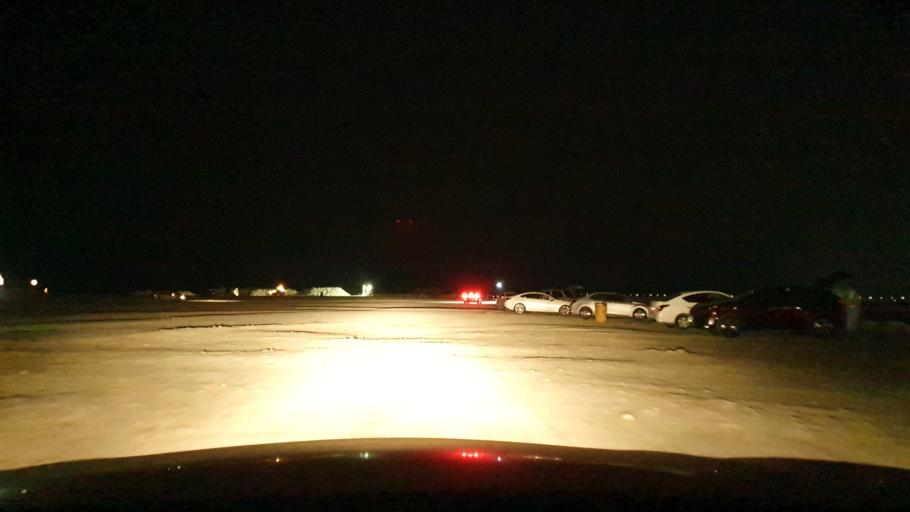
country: BH
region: Muharraq
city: Al Muharraq
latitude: 26.2543
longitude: 50.5842
